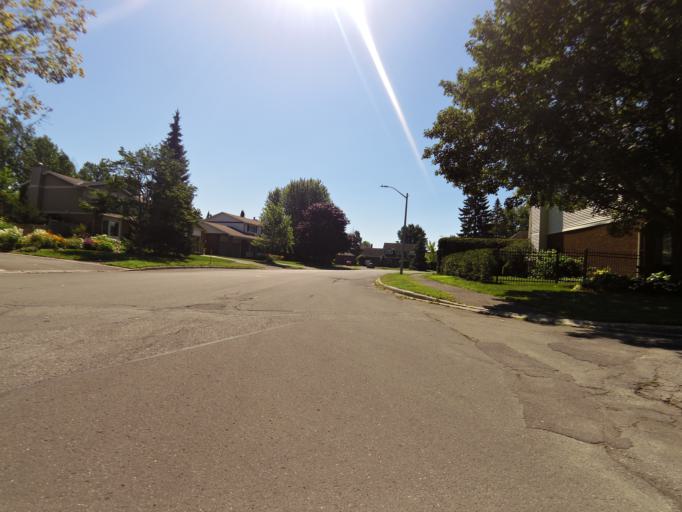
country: CA
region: Ontario
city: Ottawa
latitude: 45.3523
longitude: -75.6583
